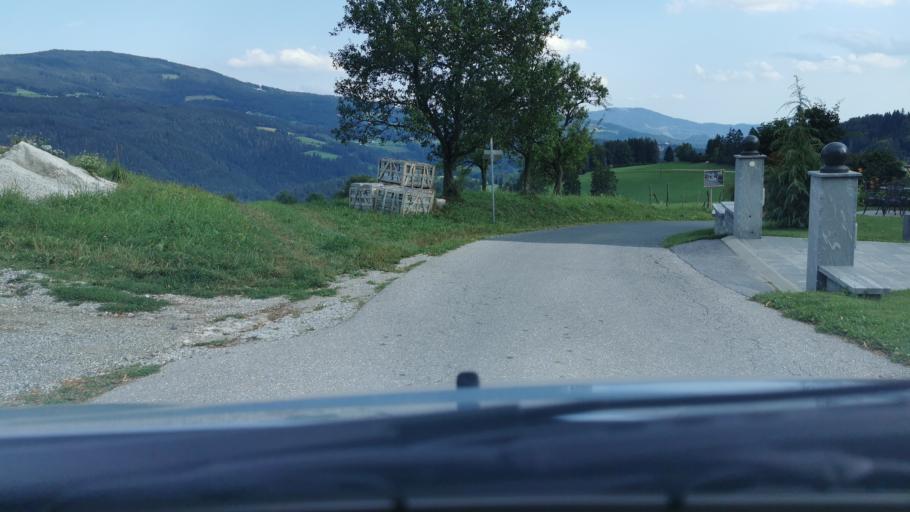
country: AT
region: Styria
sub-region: Politischer Bezirk Weiz
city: Koglhof
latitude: 47.3171
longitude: 15.6721
